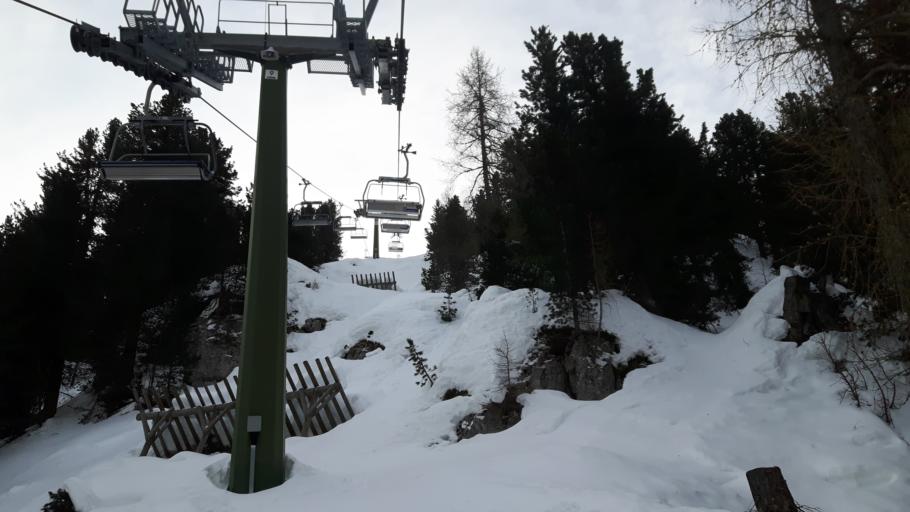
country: IT
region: Trentino-Alto Adige
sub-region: Provincia di Trento
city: Panchia
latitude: 46.3378
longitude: 11.5443
